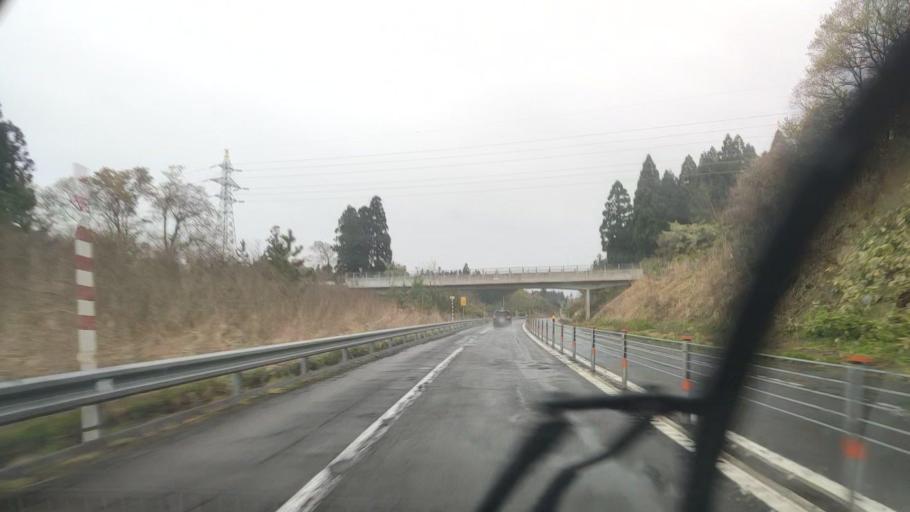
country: JP
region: Akita
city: Noshiromachi
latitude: 40.1680
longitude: 140.0507
